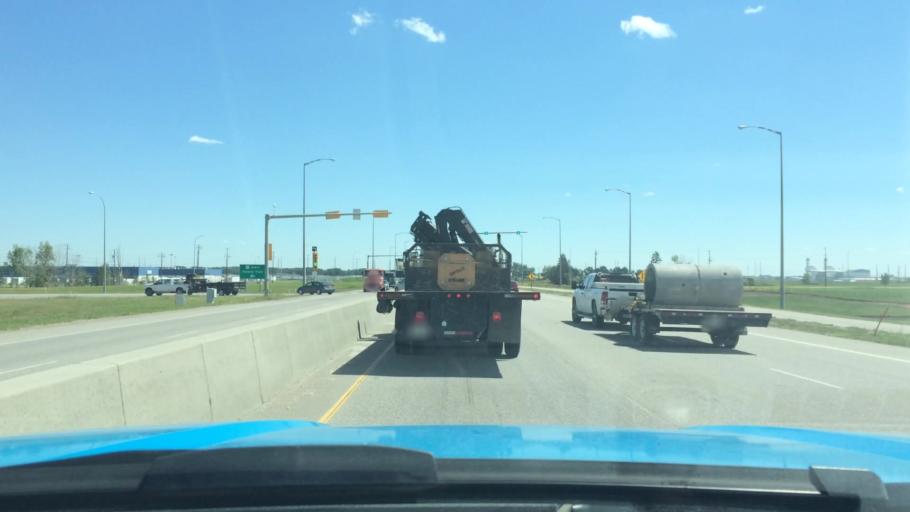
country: CA
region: Alberta
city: Chestermere
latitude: 50.9796
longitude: -113.9165
